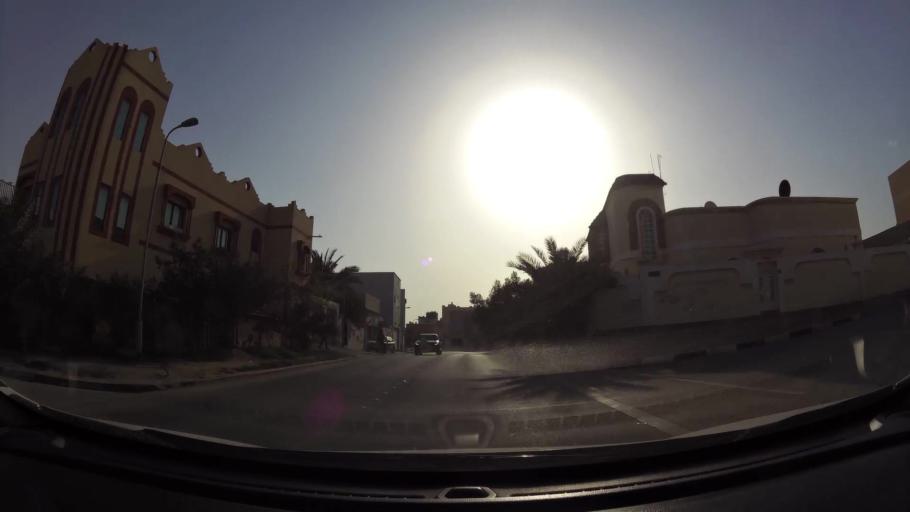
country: BH
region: Manama
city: Jidd Hafs
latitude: 26.2112
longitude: 50.5052
